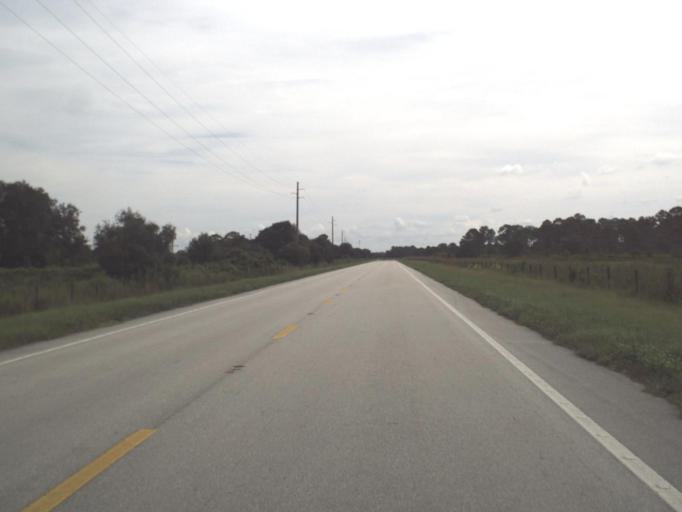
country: US
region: Florida
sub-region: Highlands County
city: Placid Lakes
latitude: 27.2088
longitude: -81.4836
